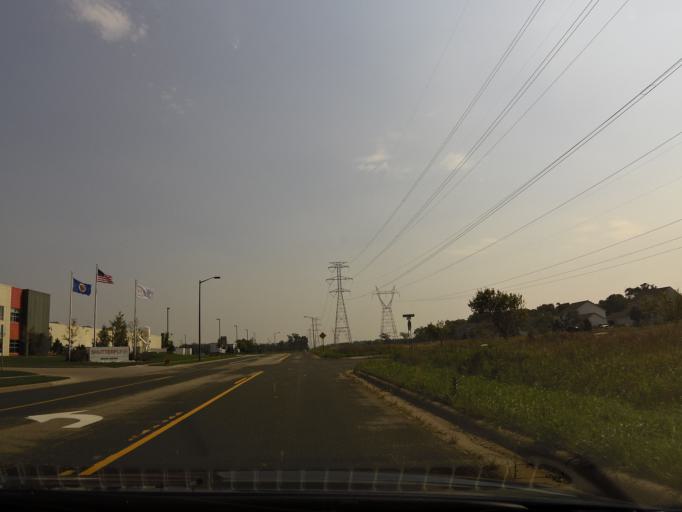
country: US
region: Minnesota
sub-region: Scott County
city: Shakopee
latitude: 44.7807
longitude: -93.4577
